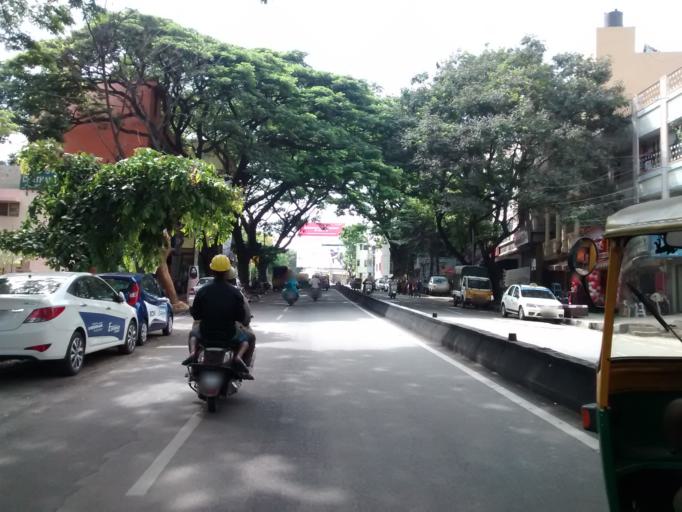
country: IN
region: Karnataka
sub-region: Bangalore Urban
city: Bangalore
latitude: 12.9951
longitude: 77.5549
